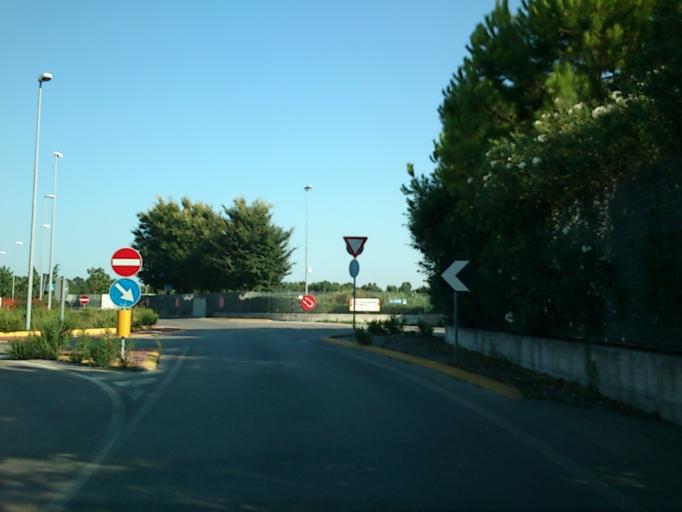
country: IT
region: The Marches
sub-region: Provincia di Pesaro e Urbino
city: Fano
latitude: 43.8267
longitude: 13.0433
